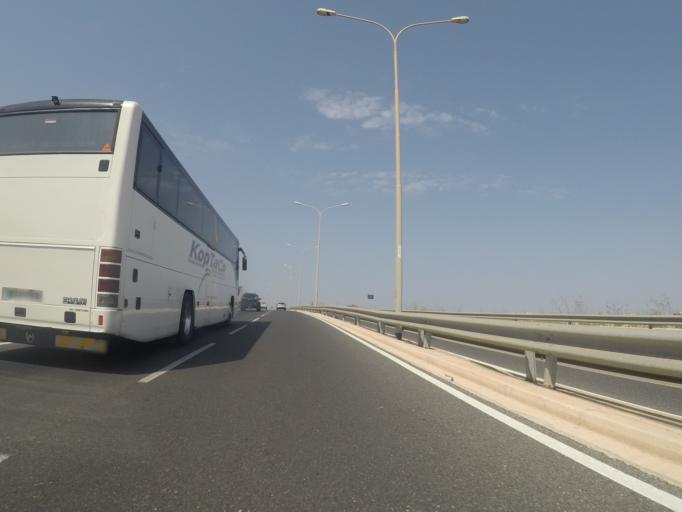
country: MT
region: Saint Paul's Bay
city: San Pawl il-Bahar
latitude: 35.9465
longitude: 14.3960
